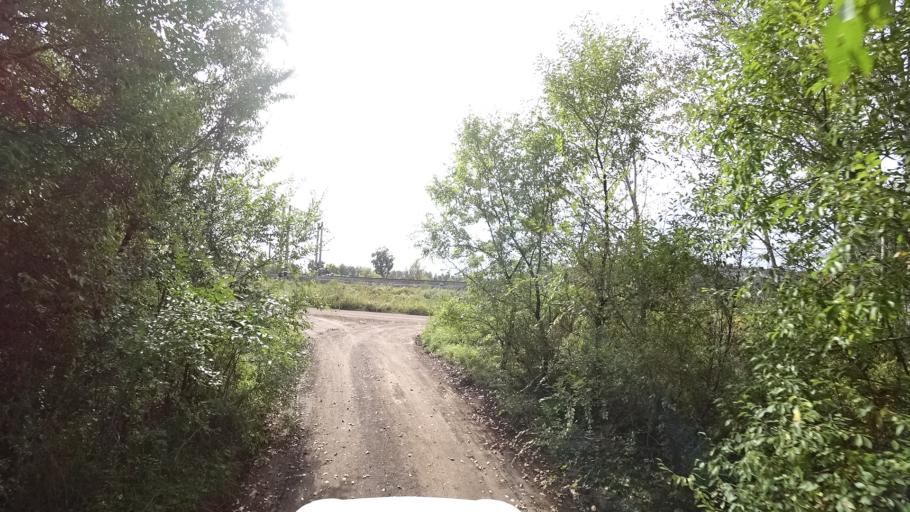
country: RU
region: Amur
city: Arkhara
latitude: 49.3525
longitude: 130.1580
